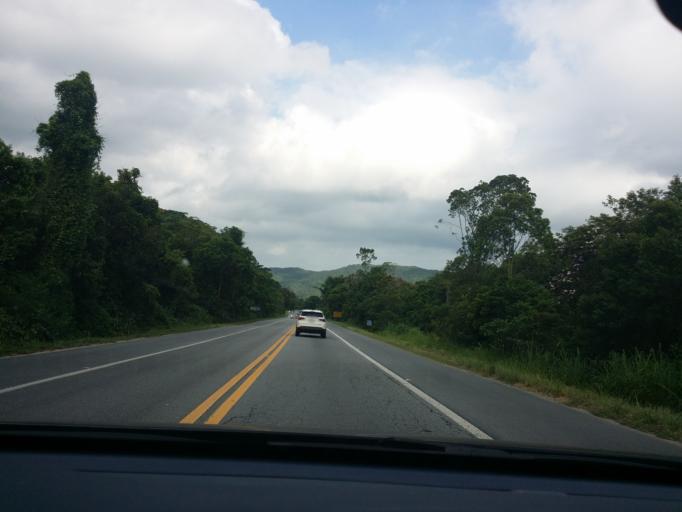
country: BR
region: Sao Paulo
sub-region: Bertioga
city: Bertioga
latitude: -23.8813
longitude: -46.1885
